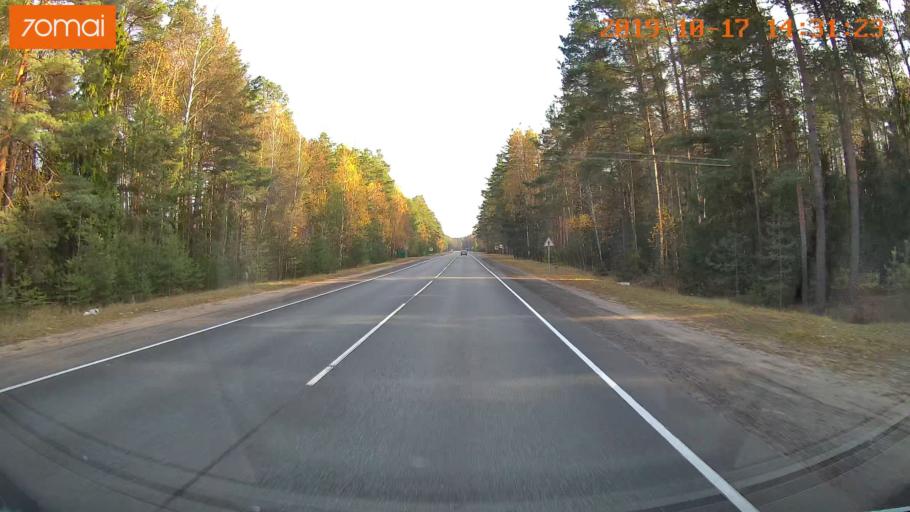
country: RU
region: Rjazan
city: Solotcha
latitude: 54.9371
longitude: 39.9617
